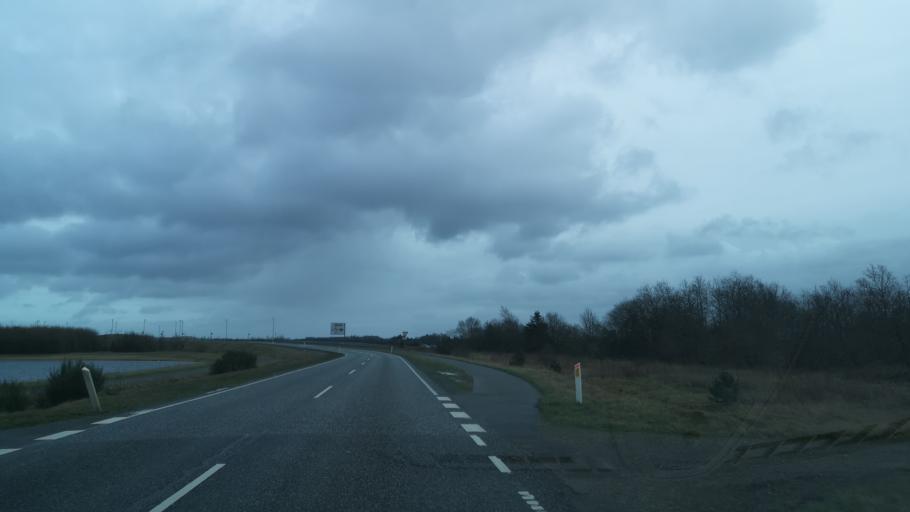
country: DK
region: Central Jutland
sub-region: Herning Kommune
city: Lind
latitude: 56.0130
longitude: 9.0175
